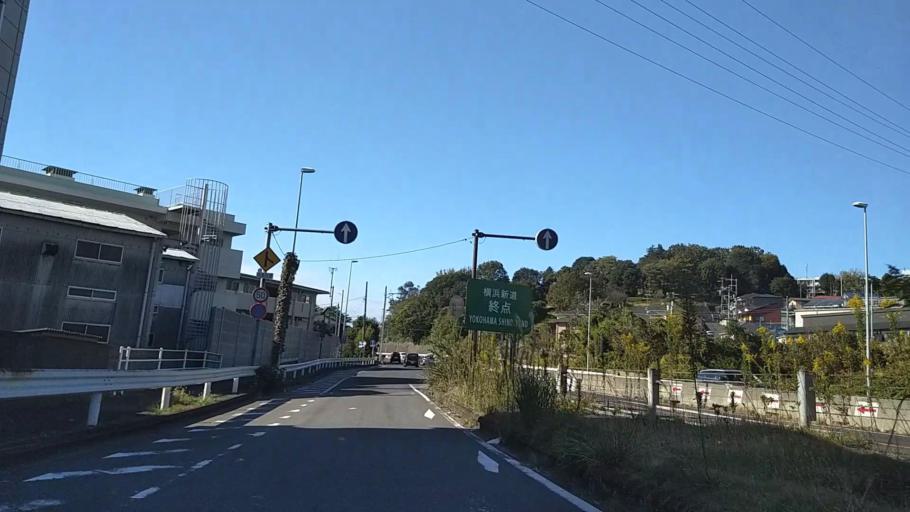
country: JP
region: Kanagawa
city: Fujisawa
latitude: 35.4128
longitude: 139.5336
